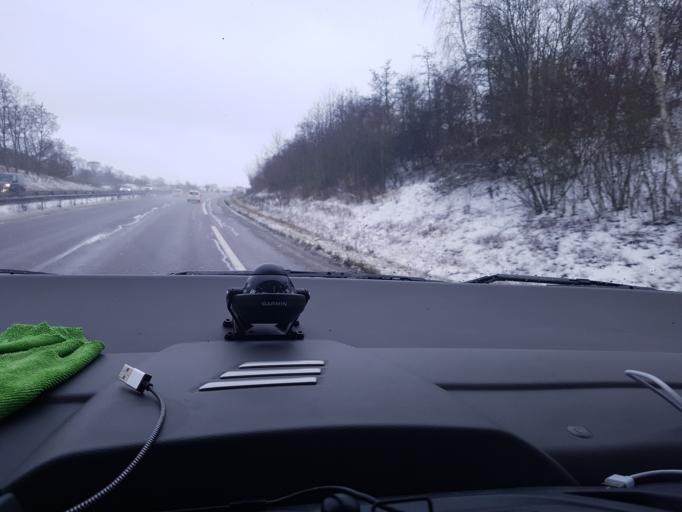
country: FR
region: Lorraine
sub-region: Departement de la Moselle
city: Argancy
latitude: 49.1760
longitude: 6.2498
